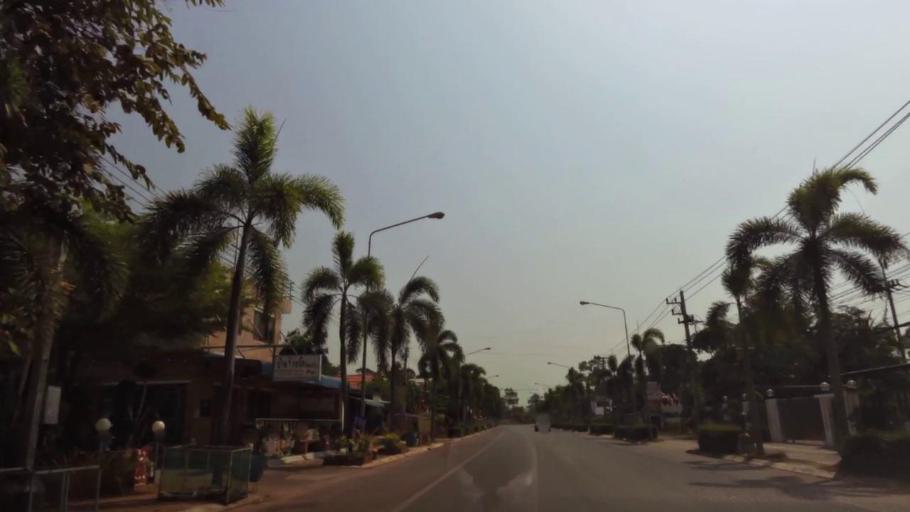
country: TH
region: Chanthaburi
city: Tha Mai
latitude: 12.5515
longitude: 101.9241
